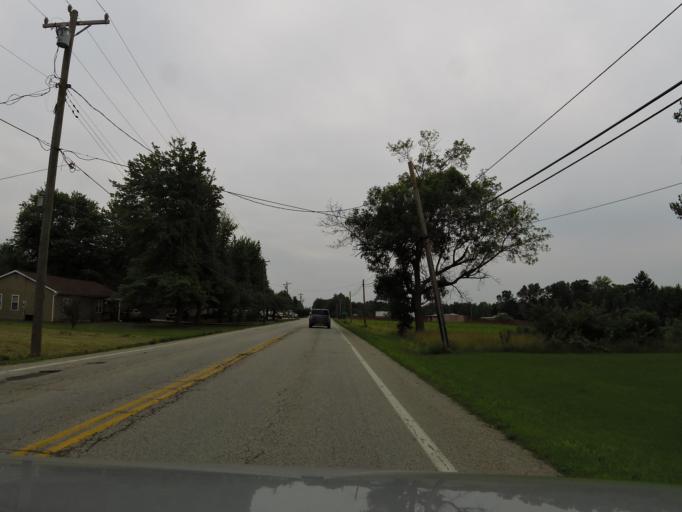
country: US
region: Ohio
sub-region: Brown County
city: Mount Orab
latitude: 39.0554
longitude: -83.9247
